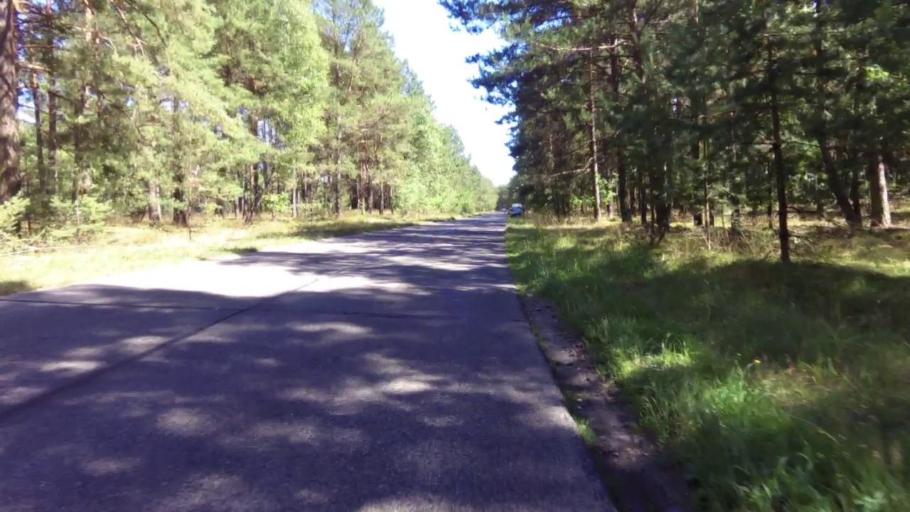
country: PL
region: West Pomeranian Voivodeship
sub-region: Powiat szczecinecki
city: Borne Sulinowo
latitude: 53.5860
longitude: 16.5011
